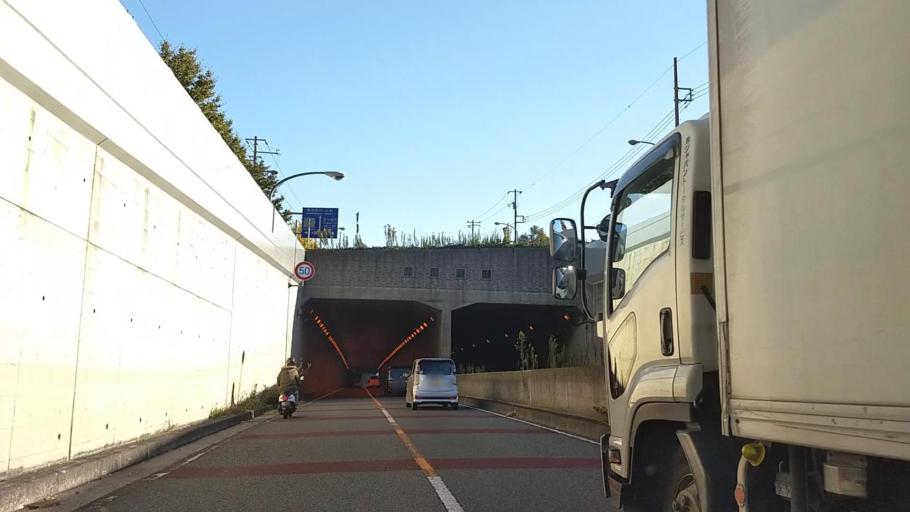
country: JP
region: Kanagawa
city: Yokohama
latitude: 35.5274
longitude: 139.5664
